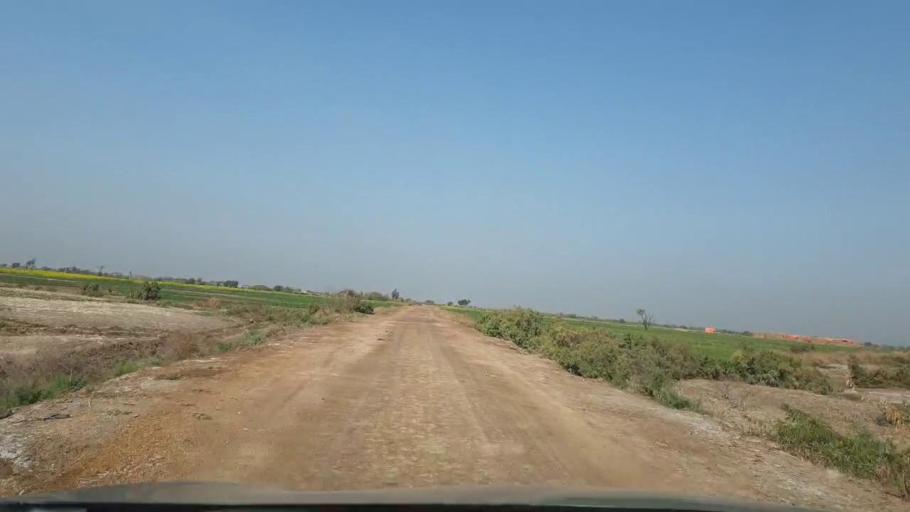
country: PK
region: Sindh
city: Berani
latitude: 25.7060
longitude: 68.8648
